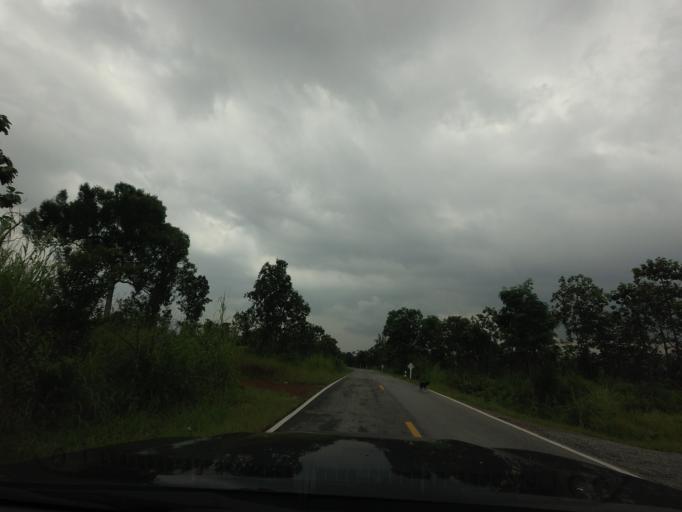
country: TH
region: Nong Khai
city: Sangkhom
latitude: 18.0364
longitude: 102.3347
